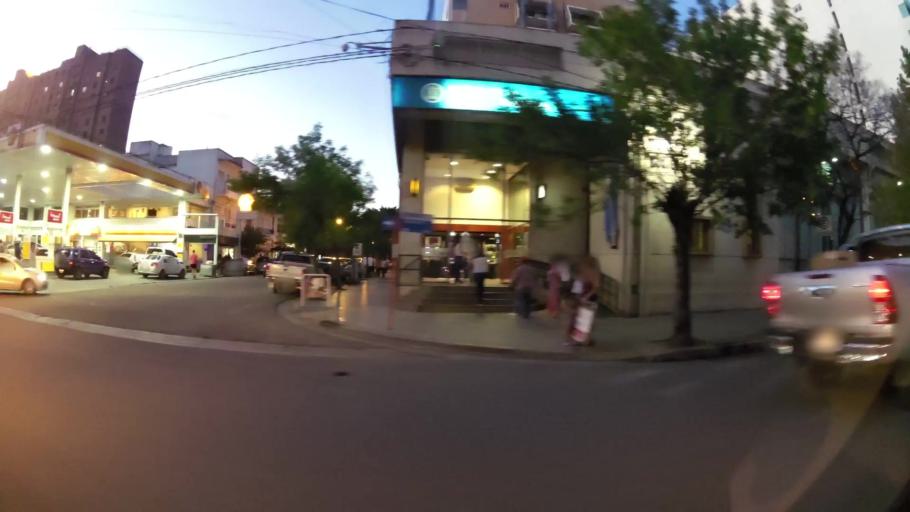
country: AR
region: Cordoba
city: Villa Maria
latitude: -32.4101
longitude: -63.2444
